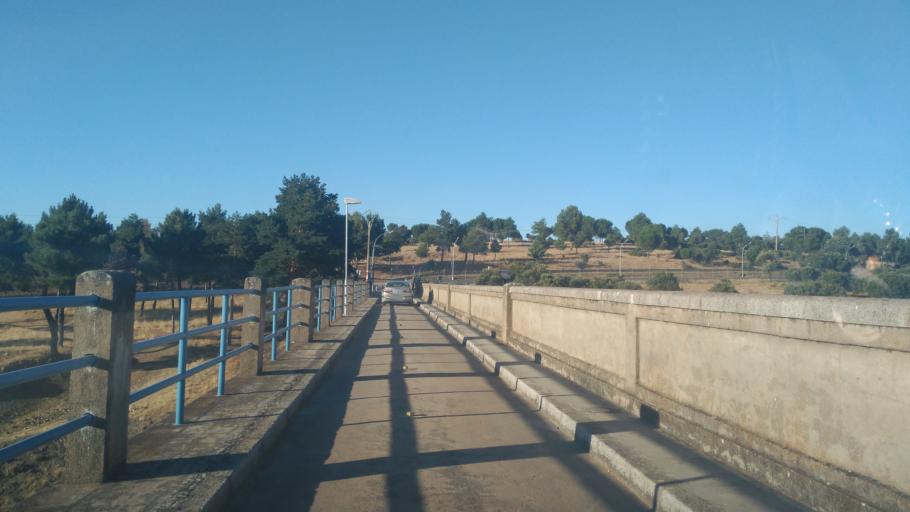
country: ES
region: Castille and Leon
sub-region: Provincia de Salamanca
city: Montejo
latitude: 40.6664
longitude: -5.6097
